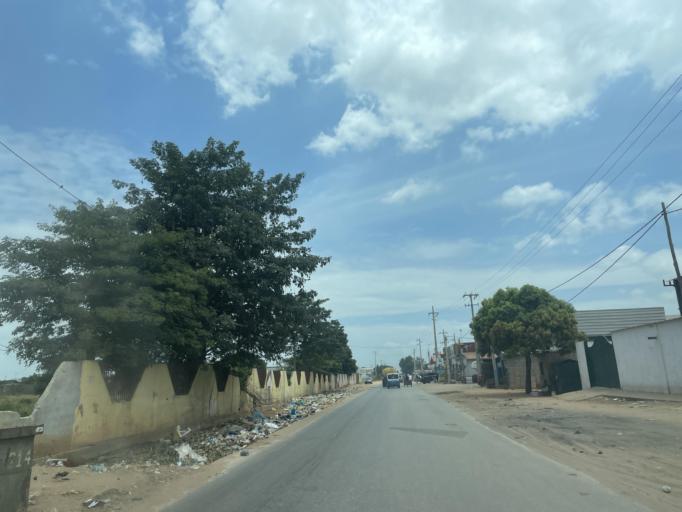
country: AO
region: Luanda
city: Luanda
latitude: -8.9300
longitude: 13.3807
